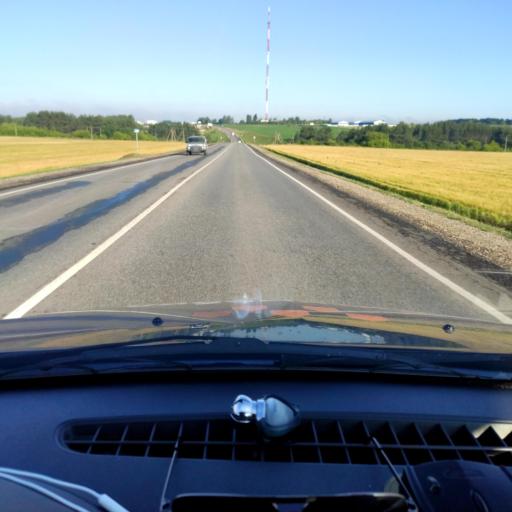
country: RU
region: Orjol
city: Livny
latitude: 52.4473
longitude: 37.5204
